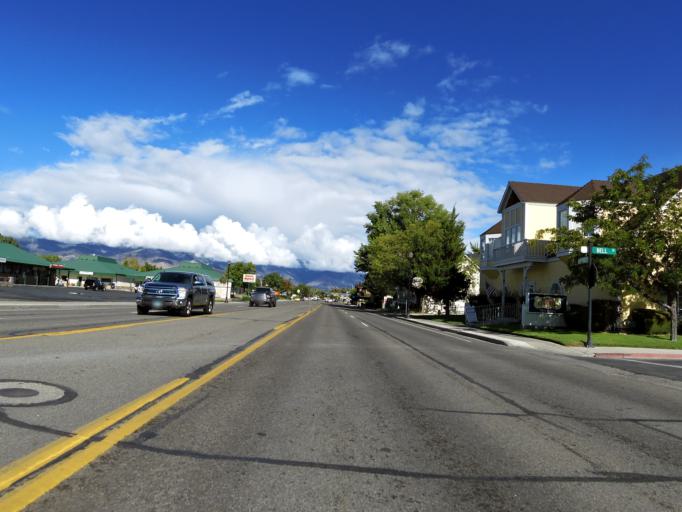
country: US
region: Nevada
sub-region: Douglas County
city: Gardnerville
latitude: 38.9469
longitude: -119.7563
